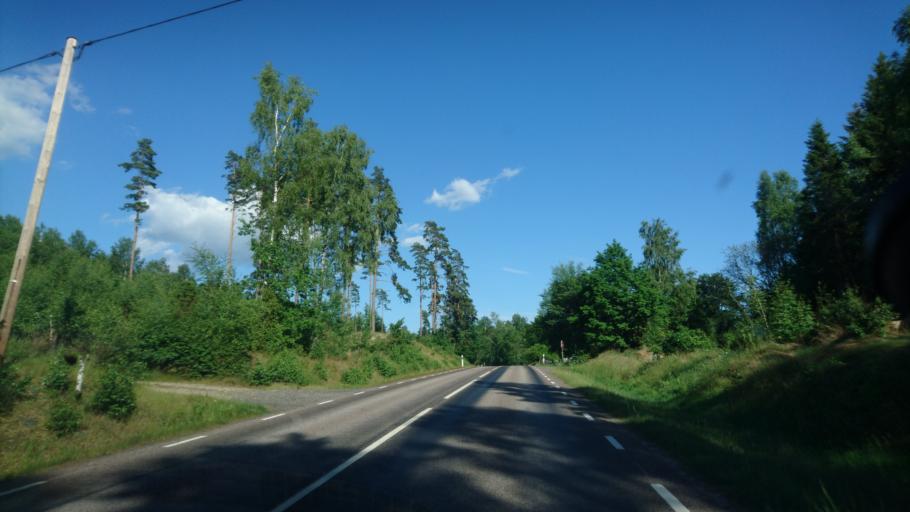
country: SE
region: Skane
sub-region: Osby Kommun
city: Lonsboda
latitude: 56.3916
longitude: 14.3390
